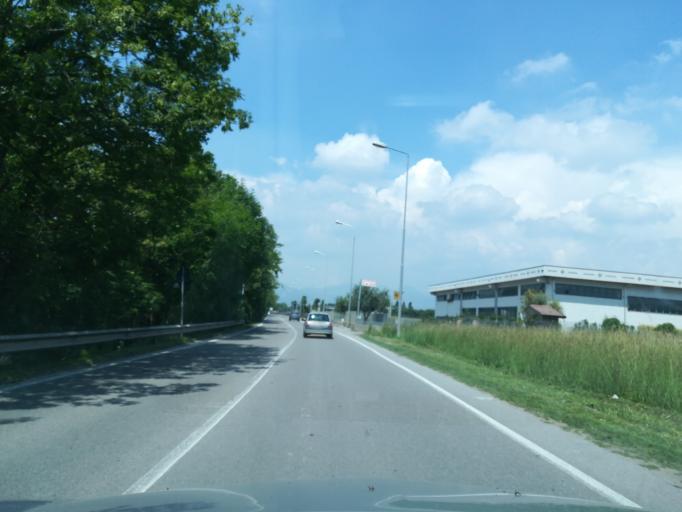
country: IT
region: Lombardy
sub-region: Provincia di Bergamo
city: Grassobbio
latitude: 45.6611
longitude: 9.7435
